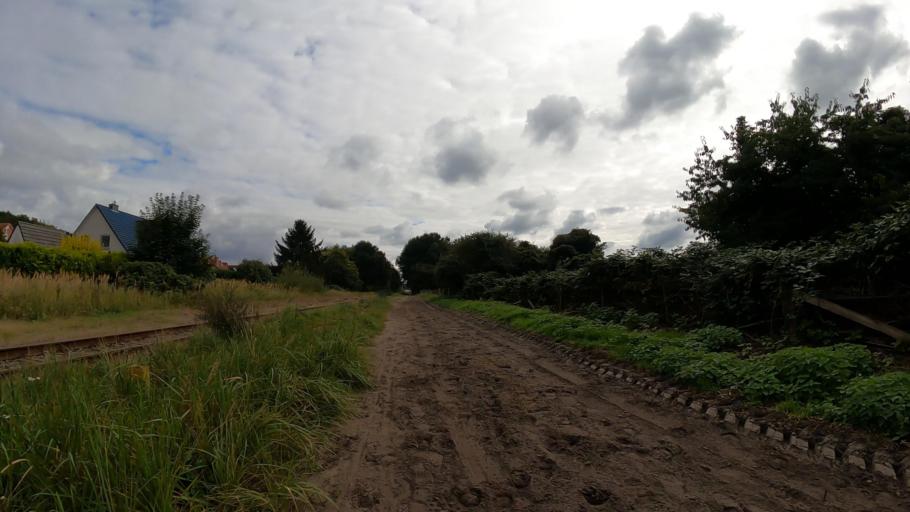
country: DE
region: Schleswig-Holstein
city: Kroppelshagen-Fahrendorf
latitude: 53.4534
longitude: 10.3484
